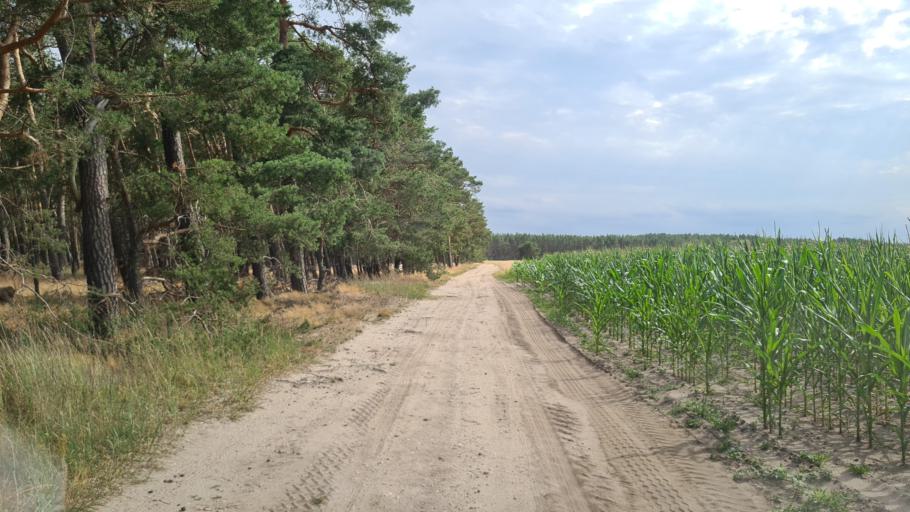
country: DE
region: Saxony-Anhalt
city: Holzdorf
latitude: 51.8173
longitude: 13.1951
